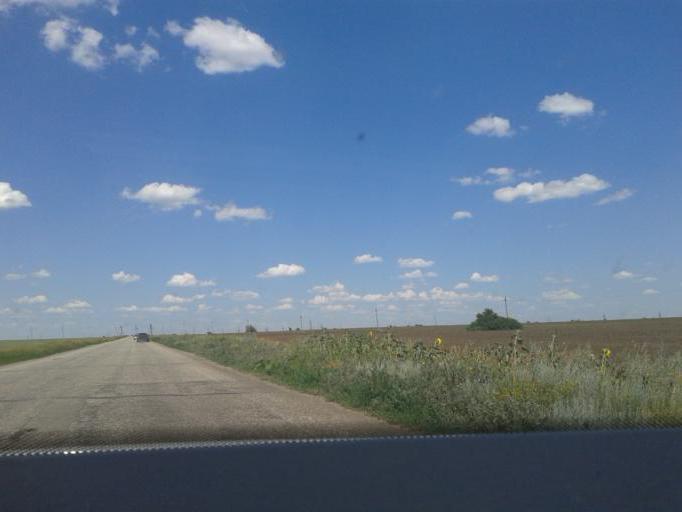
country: RU
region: Volgograd
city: Frolovo
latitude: 49.6995
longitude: 43.6515
